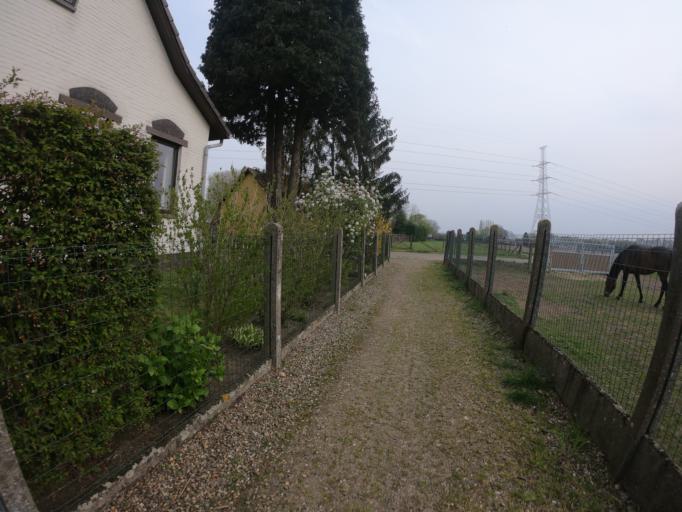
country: BE
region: Flanders
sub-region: Provincie Limburg
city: Maaseik
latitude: 51.0650
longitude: 5.7202
